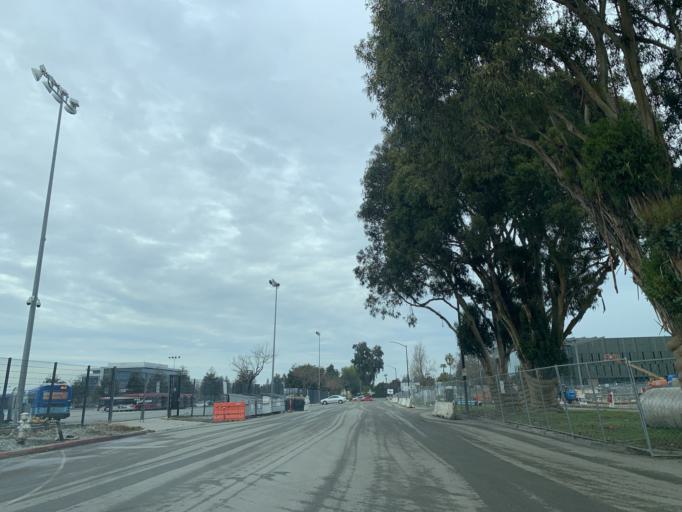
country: US
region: California
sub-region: Santa Clara County
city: Mountain View
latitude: 37.4116
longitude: -122.0734
